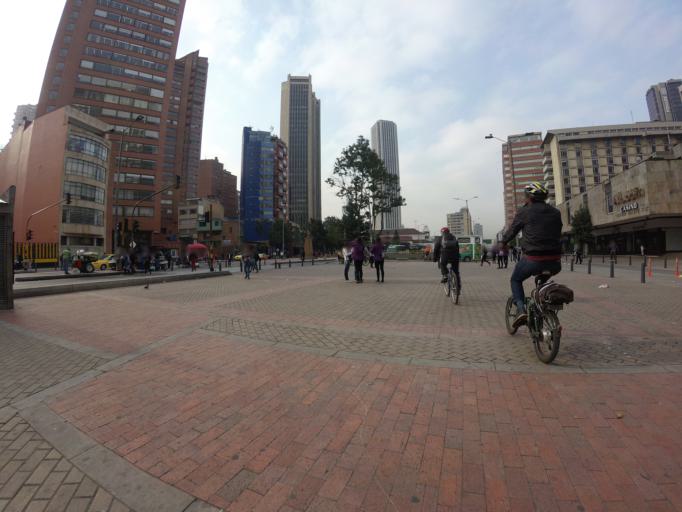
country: CO
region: Bogota D.C.
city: Bogota
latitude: 4.6140
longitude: -74.0697
